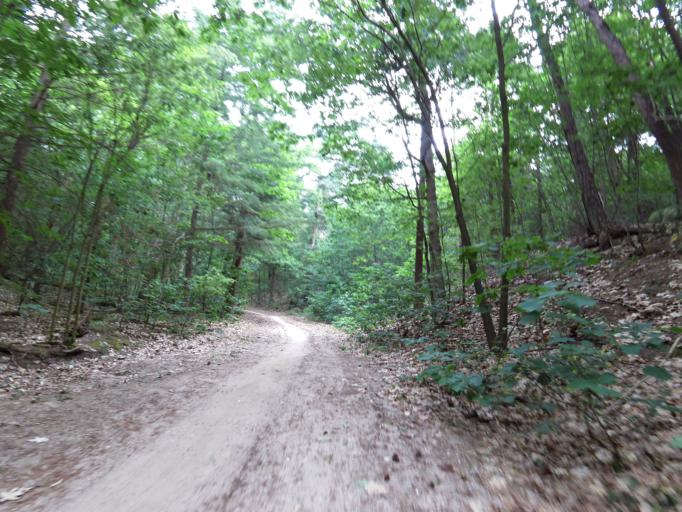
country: NL
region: North Brabant
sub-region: Gemeente Cuijk
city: Cuijk
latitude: 51.7566
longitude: 5.8859
